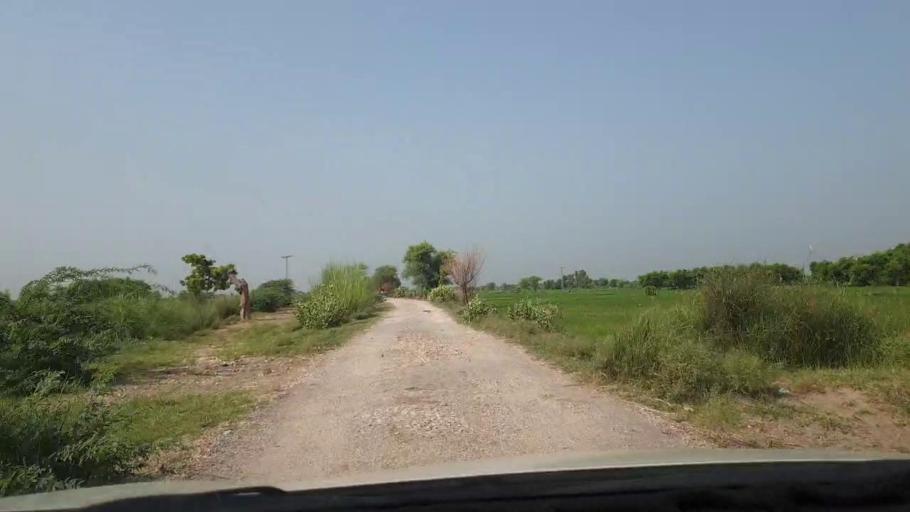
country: PK
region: Sindh
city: Goth Garelo
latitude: 27.4617
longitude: 68.1283
